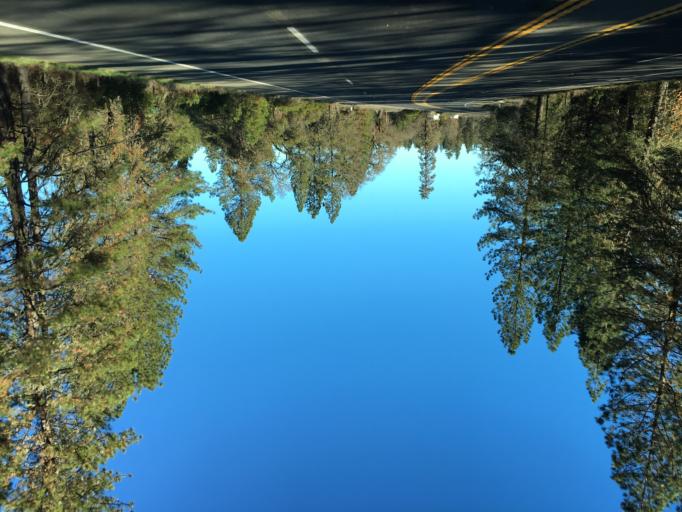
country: US
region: California
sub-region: Mendocino County
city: Laytonville
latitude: 39.7264
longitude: -123.5042
